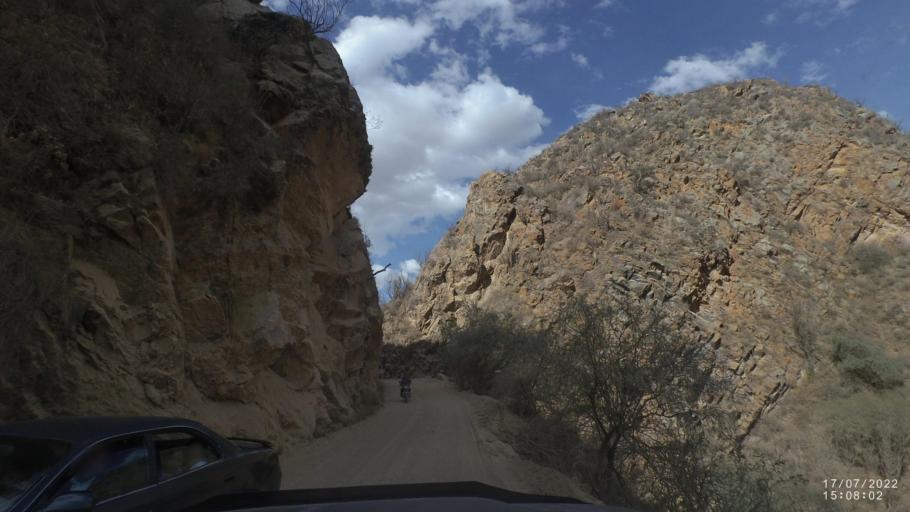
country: BO
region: Cochabamba
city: Capinota
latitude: -17.5800
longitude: -66.2684
